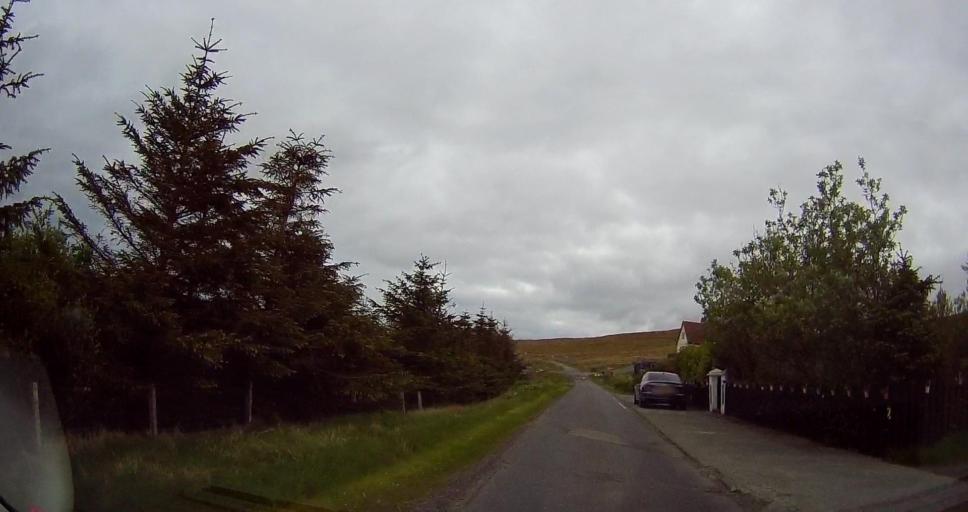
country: GB
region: Scotland
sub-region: Shetland Islands
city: Shetland
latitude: 60.5965
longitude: -1.0745
